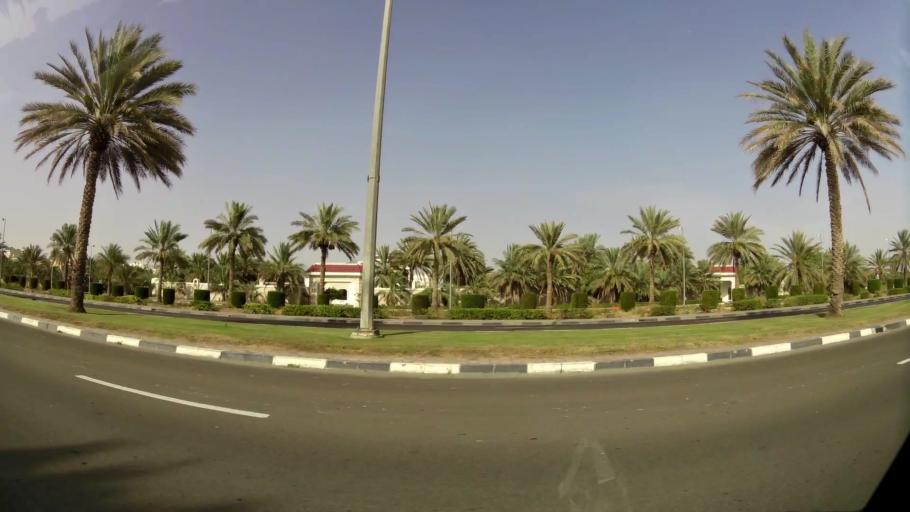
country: AE
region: Abu Dhabi
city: Al Ain
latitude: 24.2193
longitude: 55.6822
